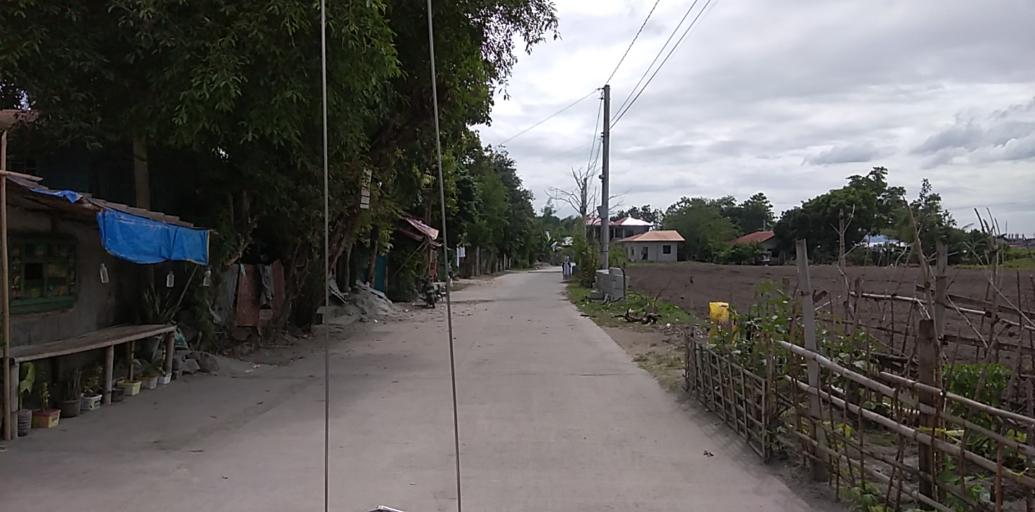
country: PH
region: Central Luzon
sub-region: Province of Pampanga
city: Porac
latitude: 15.0649
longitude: 120.5396
